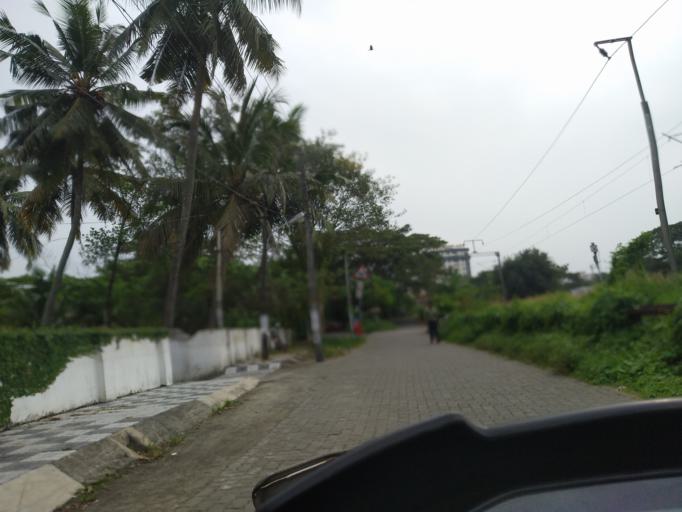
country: IN
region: Kerala
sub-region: Ernakulam
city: Cochin
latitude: 9.9534
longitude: 76.2945
